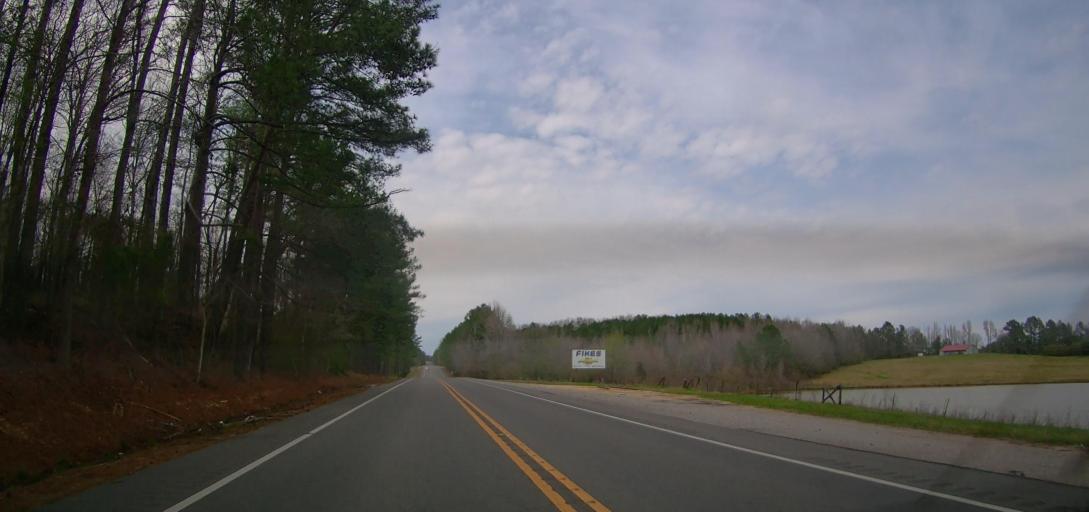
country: US
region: Alabama
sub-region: Marion County
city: Guin
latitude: 34.0104
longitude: -87.9350
